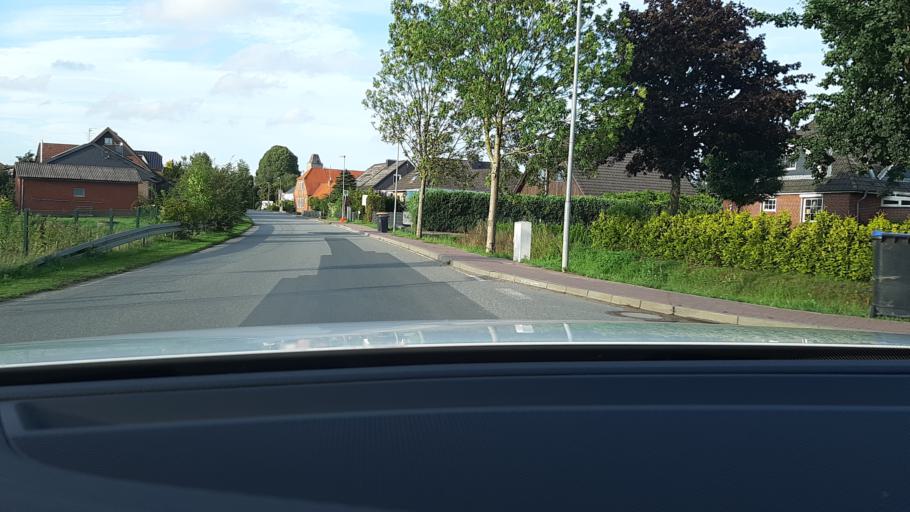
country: DE
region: Schleswig-Holstein
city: Monkhagen
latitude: 53.9361
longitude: 10.5964
